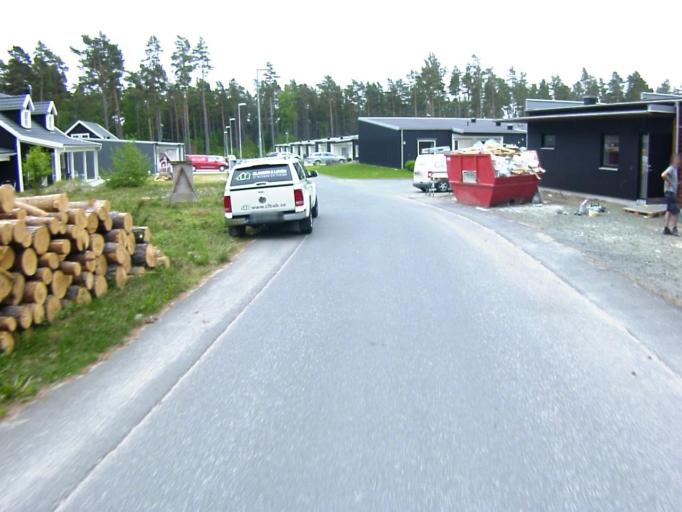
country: SE
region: Skane
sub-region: Kristianstads Kommun
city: Ahus
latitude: 55.9091
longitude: 14.2736
